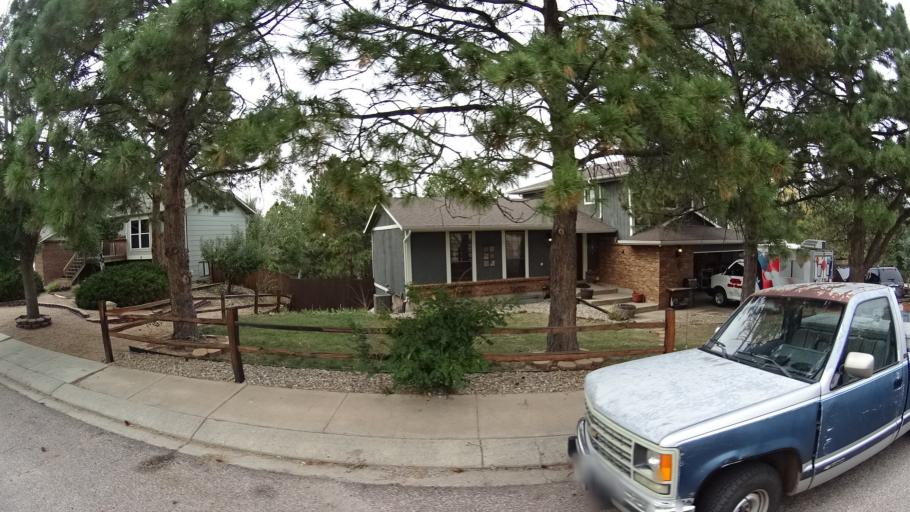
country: US
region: Colorado
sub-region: El Paso County
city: Cimarron Hills
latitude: 38.9003
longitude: -104.7250
